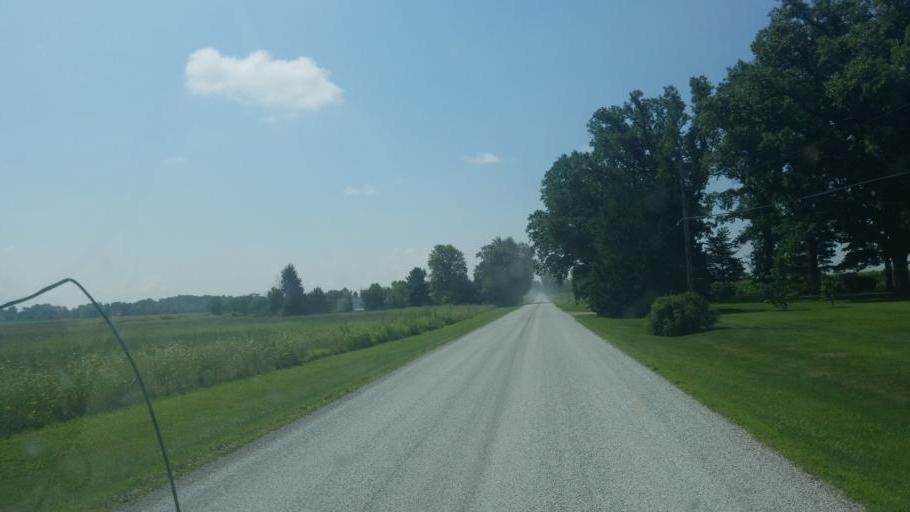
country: US
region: Ohio
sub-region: Hardin County
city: Kenton
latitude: 40.6824
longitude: -83.7301
